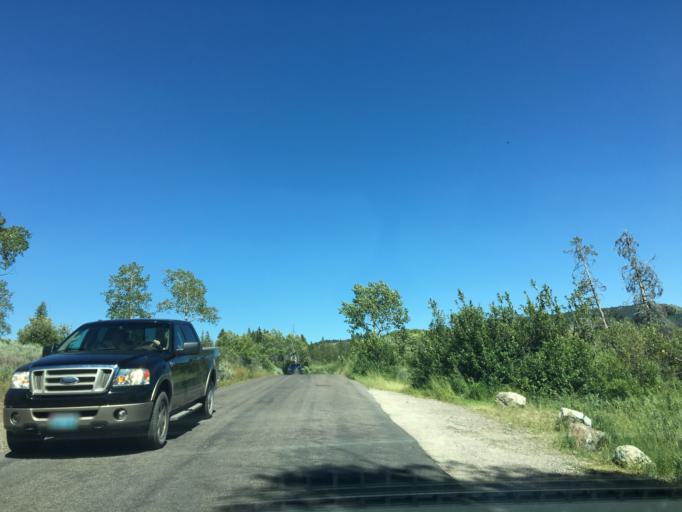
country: US
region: Wyoming
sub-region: Teton County
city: Moose Wilson Road
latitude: 43.6509
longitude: -110.7473
